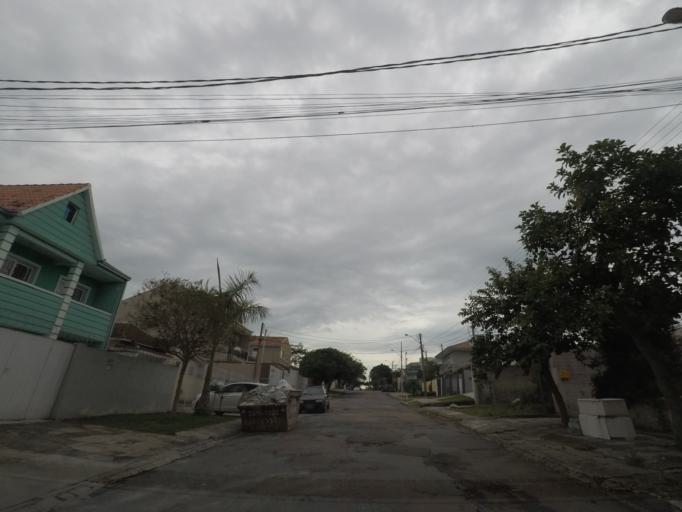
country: BR
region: Parana
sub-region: Curitiba
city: Curitiba
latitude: -25.4678
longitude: -49.3048
